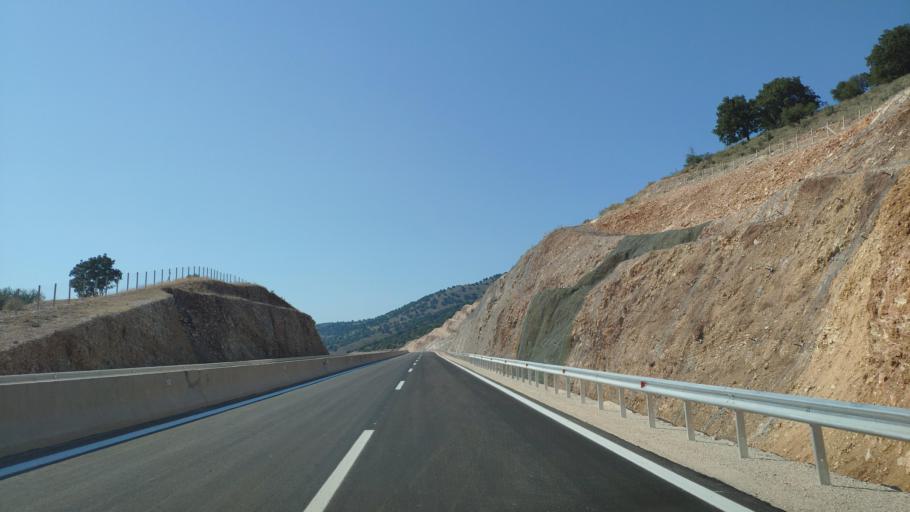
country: GR
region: West Greece
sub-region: Nomos Aitolias kai Akarnanias
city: Katouna
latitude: 38.8162
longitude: 21.1276
